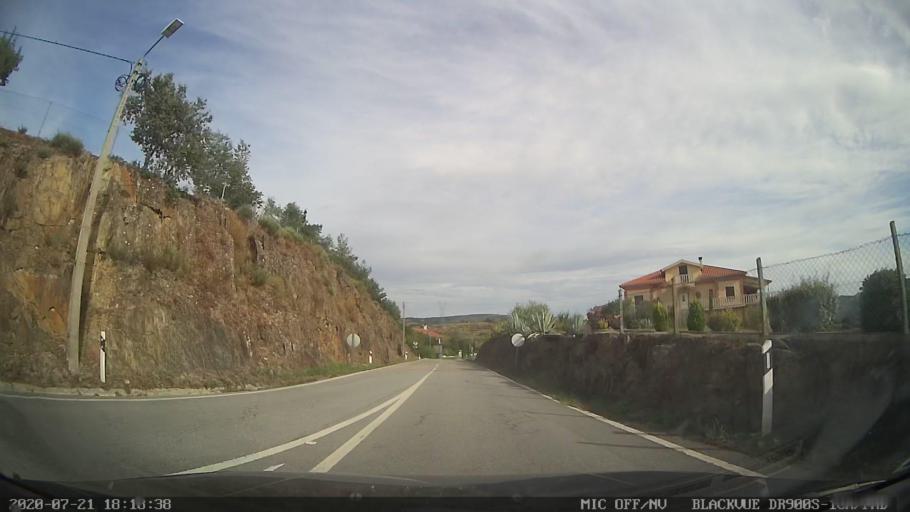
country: PT
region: Guarda
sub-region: Vila Nova de Foz Coa
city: Custoias
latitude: 41.0960
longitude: -7.3740
